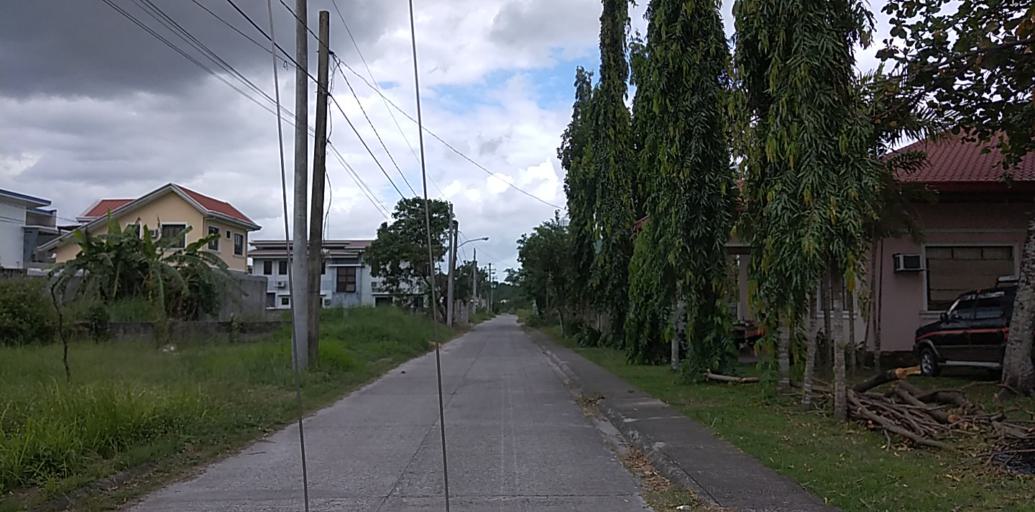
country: PH
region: Central Luzon
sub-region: Province of Pampanga
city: Porac
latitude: 15.0638
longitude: 120.5450
